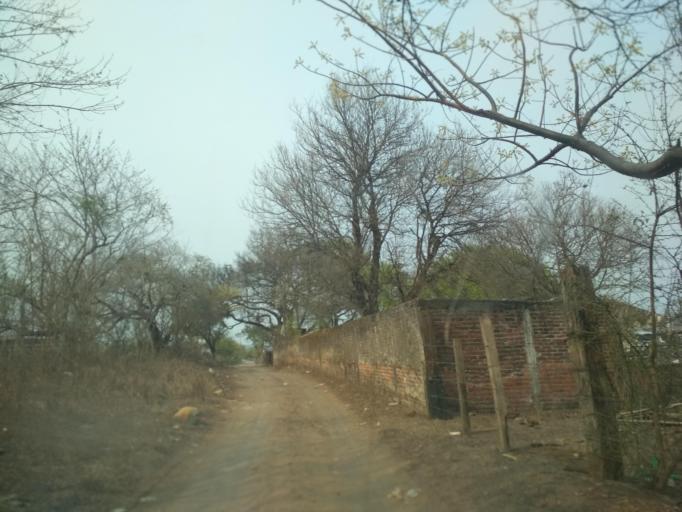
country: MX
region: Veracruz
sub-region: Veracruz
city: Delfino Victoria (Santa Fe)
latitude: 19.1968
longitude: -96.2961
